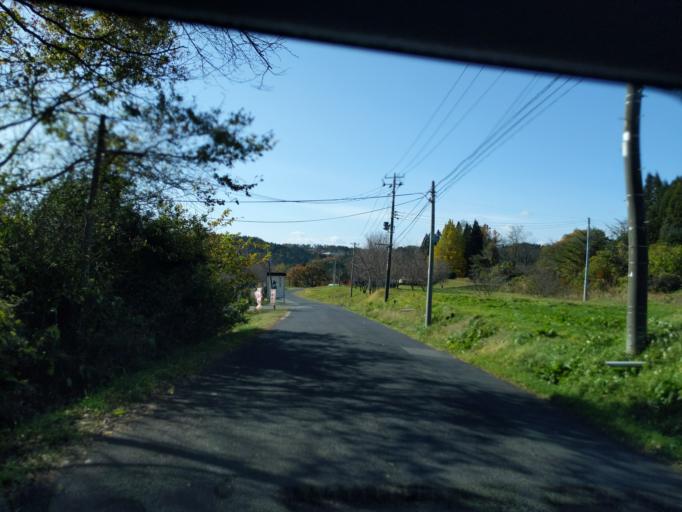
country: JP
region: Iwate
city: Mizusawa
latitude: 39.0310
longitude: 141.1083
